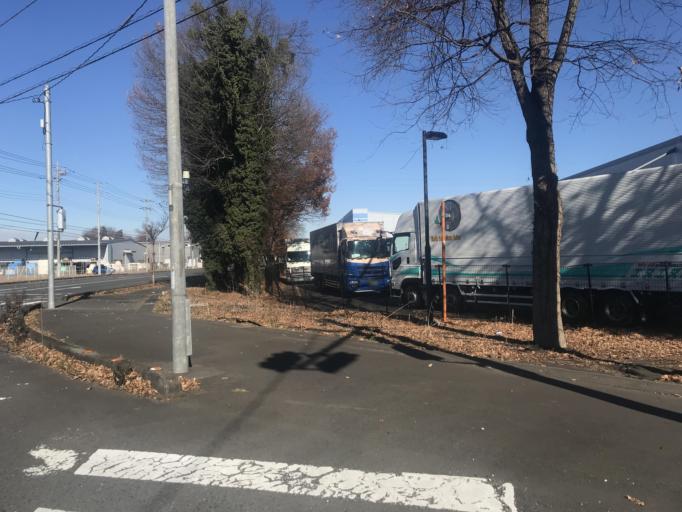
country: JP
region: Ibaraki
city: Yuki
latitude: 36.3288
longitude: 139.8799
